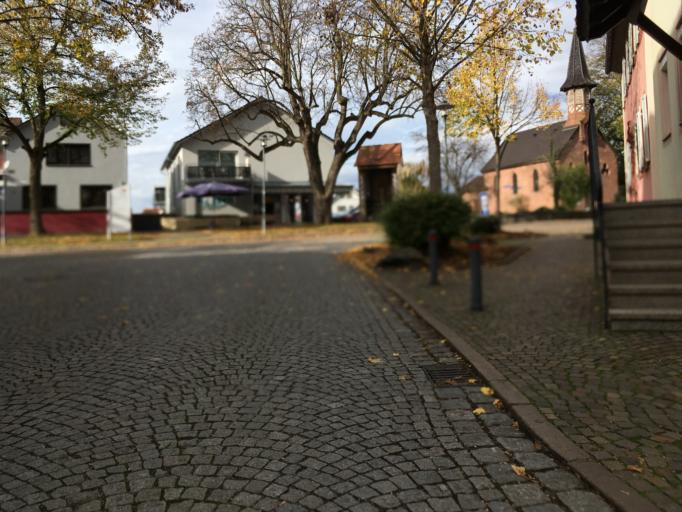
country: DE
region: Baden-Wuerttemberg
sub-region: Freiburg Region
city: Riegel
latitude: 48.1517
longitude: 7.7483
